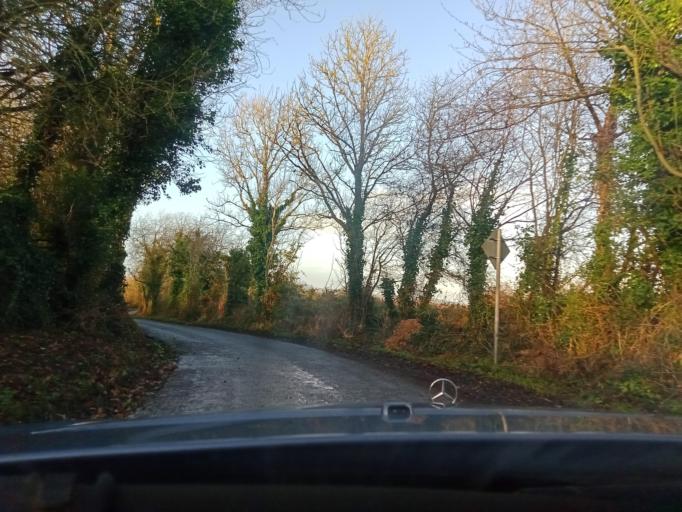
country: IE
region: Leinster
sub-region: Kilkenny
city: Callan
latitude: 52.4771
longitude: -7.4484
